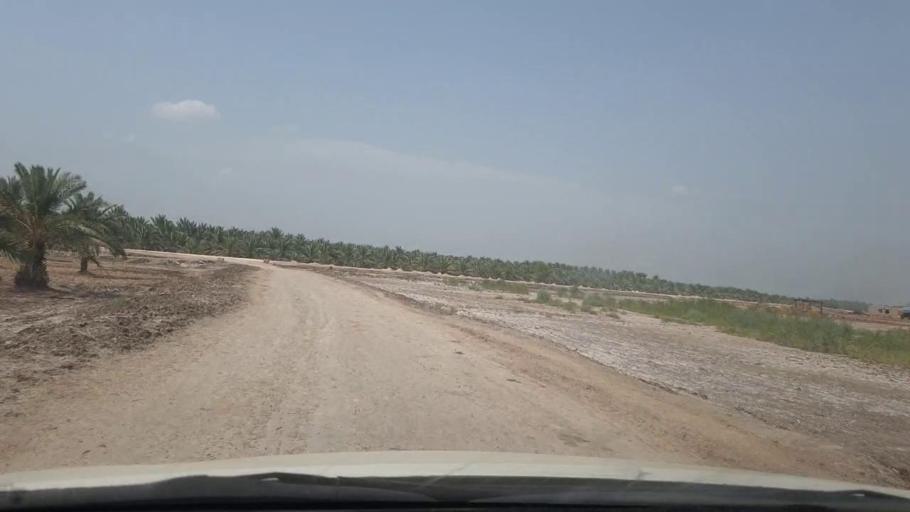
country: PK
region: Sindh
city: Khairpur
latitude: 27.5650
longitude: 68.8428
